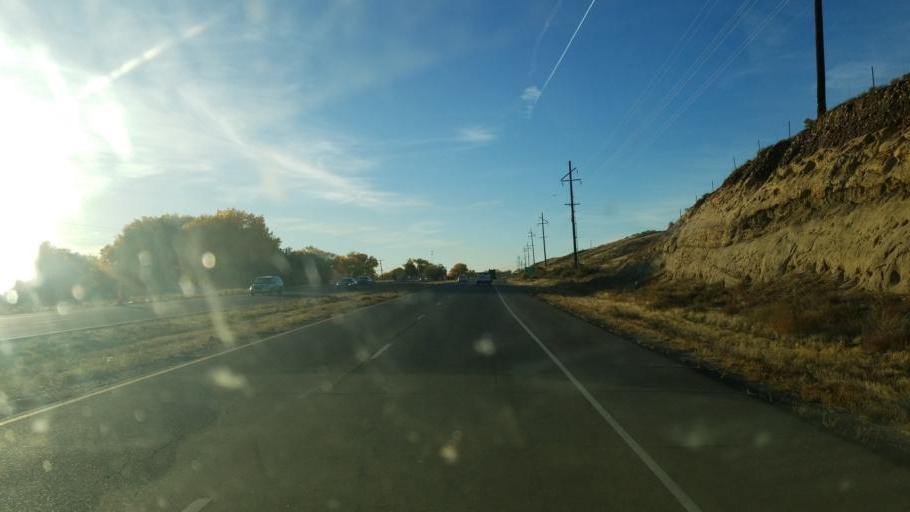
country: US
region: New Mexico
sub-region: San Juan County
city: Farmington
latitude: 36.7083
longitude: -108.1290
